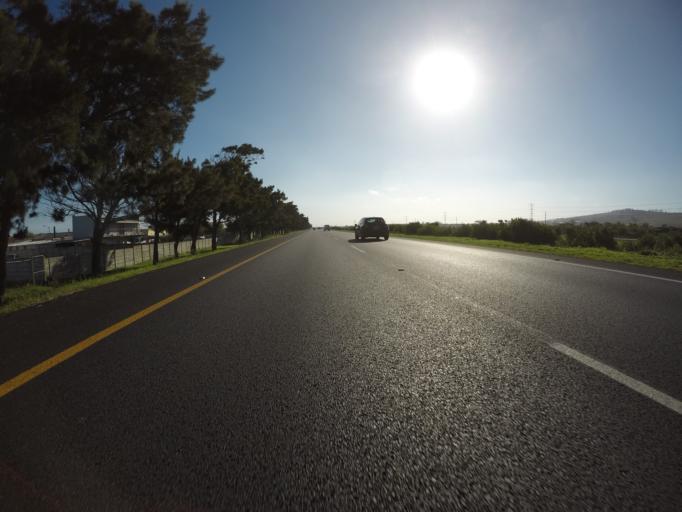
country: ZA
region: Western Cape
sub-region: Cape Winelands District Municipality
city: Stellenbosch
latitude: -34.0556
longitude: 18.7684
